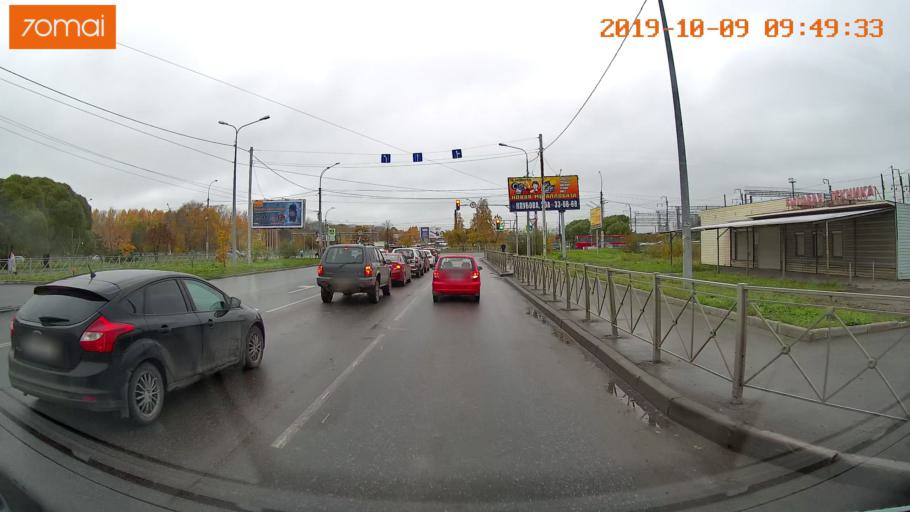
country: RU
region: Vologda
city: Vologda
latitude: 59.1986
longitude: 39.9127
